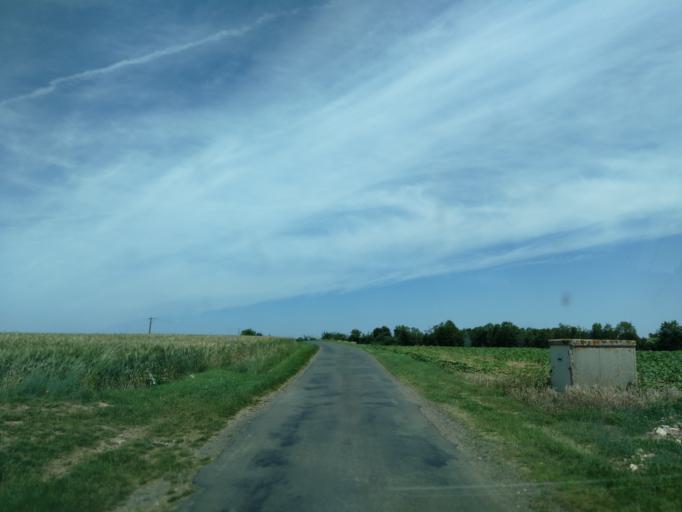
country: FR
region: Pays de la Loire
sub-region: Departement de la Vendee
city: Le Langon
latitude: 46.4245
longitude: -0.8957
